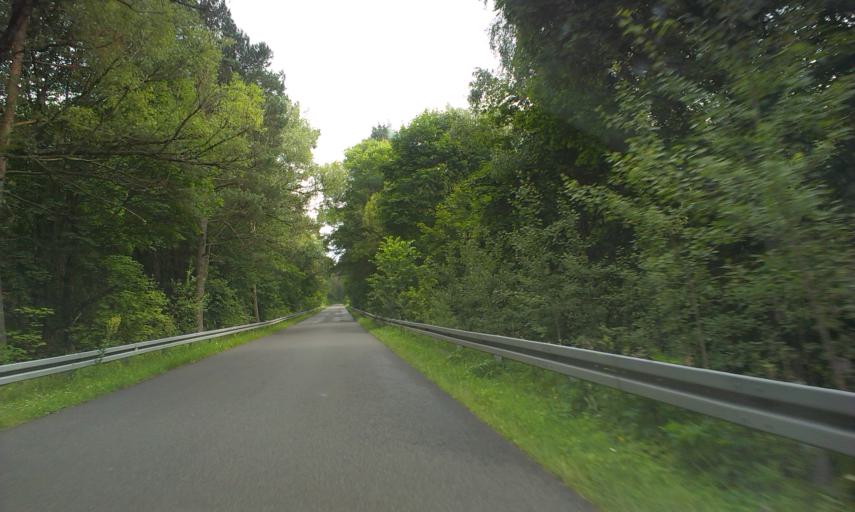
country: PL
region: Greater Poland Voivodeship
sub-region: Powiat zlotowski
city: Zlotow
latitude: 53.4913
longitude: 16.9865
